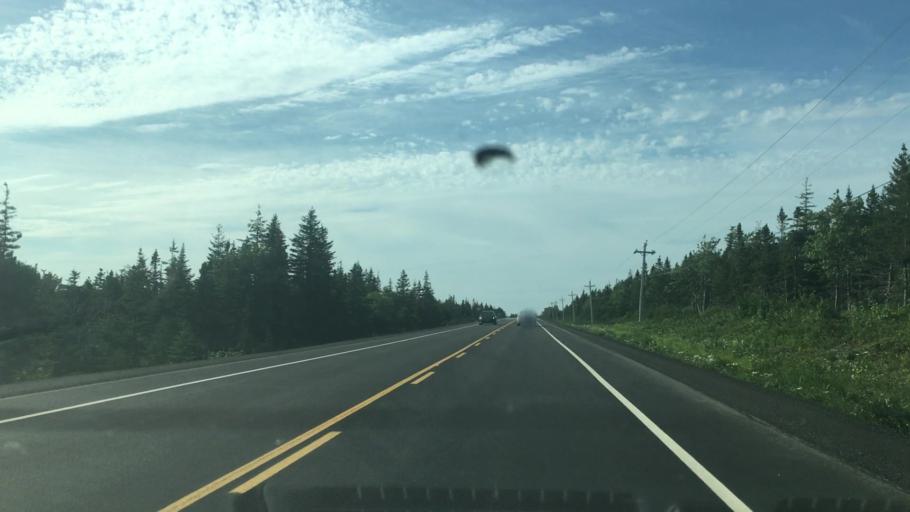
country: CA
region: Nova Scotia
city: Sydney Mines
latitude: 46.8453
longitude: -60.4089
